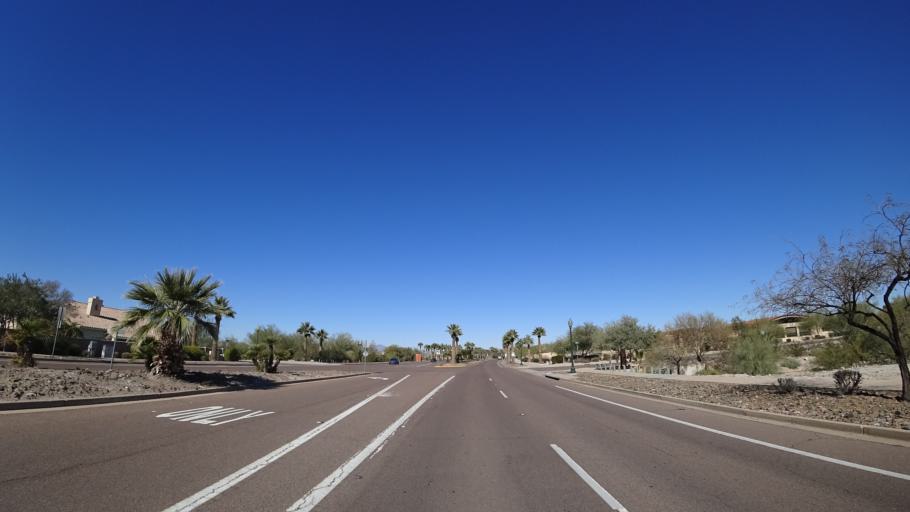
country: US
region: Arizona
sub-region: Maricopa County
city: Goodyear
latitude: 33.3487
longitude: -112.4279
